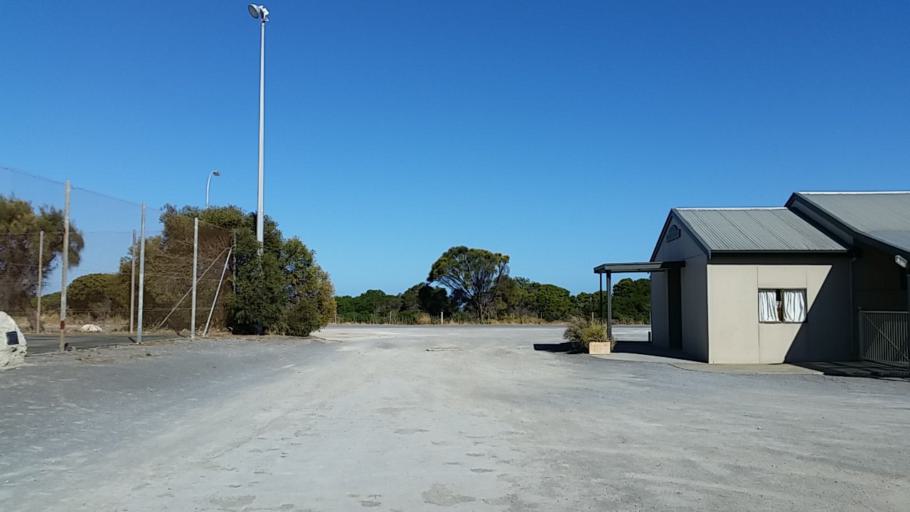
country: AU
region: South Australia
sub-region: Yorke Peninsula
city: Honiton
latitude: -35.2377
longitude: 136.9806
